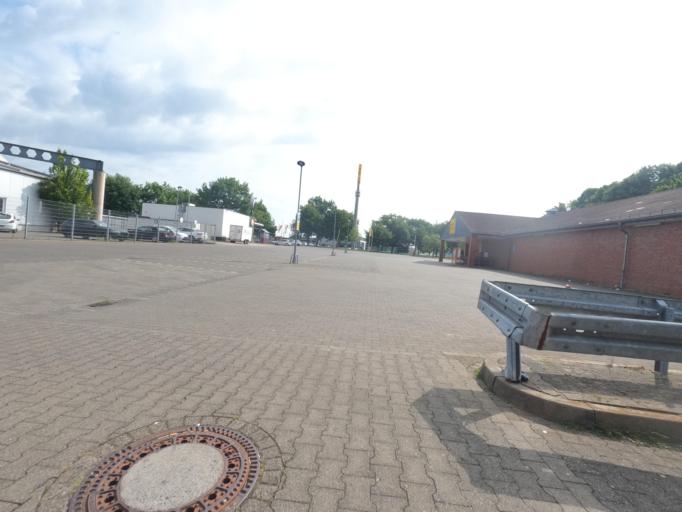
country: DE
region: North Rhine-Westphalia
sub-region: Regierungsbezirk Koln
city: Heinsberg
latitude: 51.0596
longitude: 6.1183
